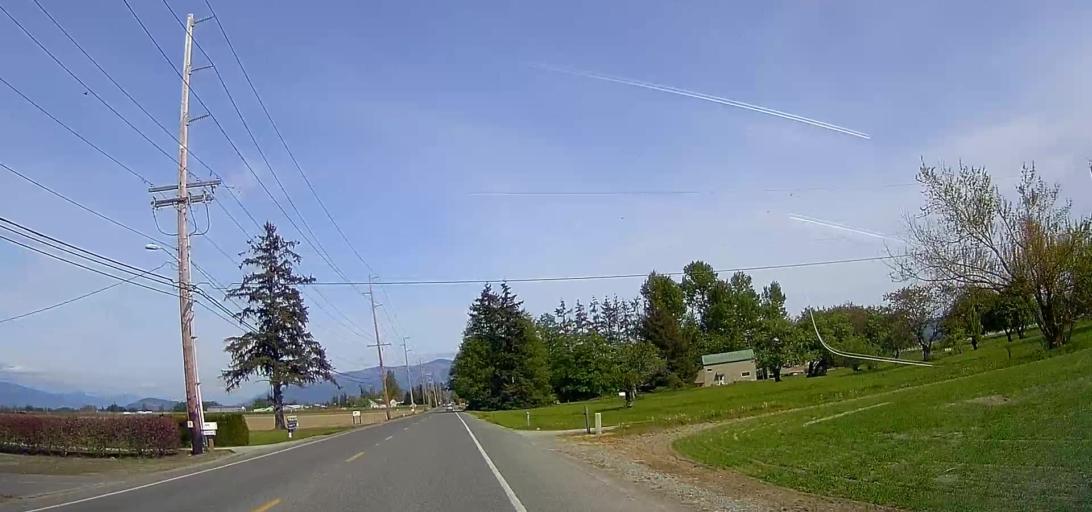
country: US
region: Washington
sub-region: Skagit County
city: Mount Vernon
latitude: 48.4208
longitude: -122.4278
